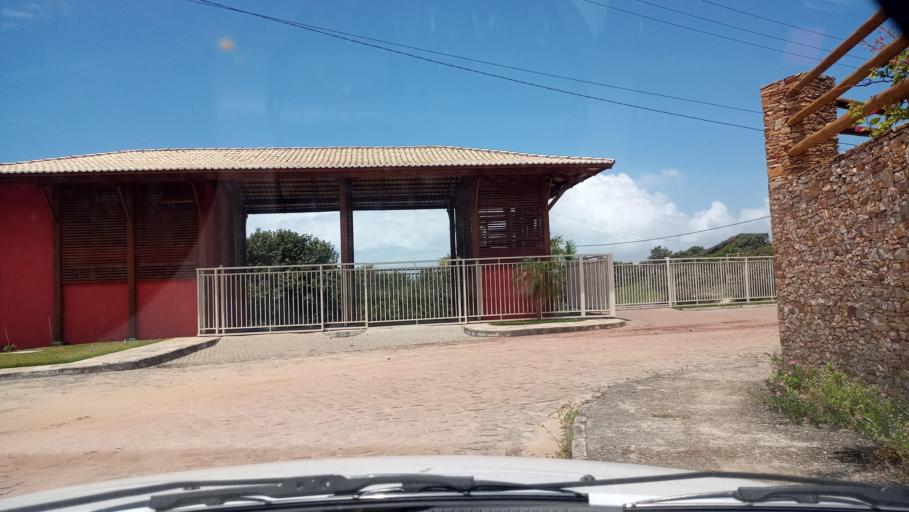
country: BR
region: Rio Grande do Norte
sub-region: Ares
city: Ares
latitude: -6.2444
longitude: -35.0430
